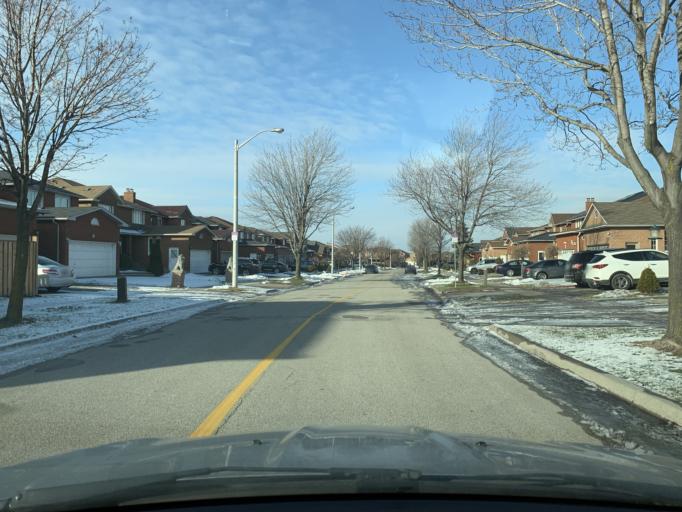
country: CA
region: Ontario
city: Etobicoke
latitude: 43.7211
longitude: -79.6191
